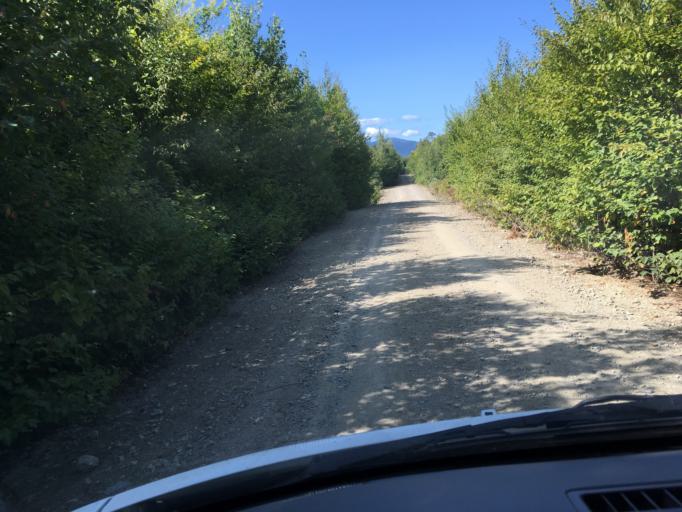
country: US
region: Maine
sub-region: Penobscot County
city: Millinocket
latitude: 45.8581
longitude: -68.7546
